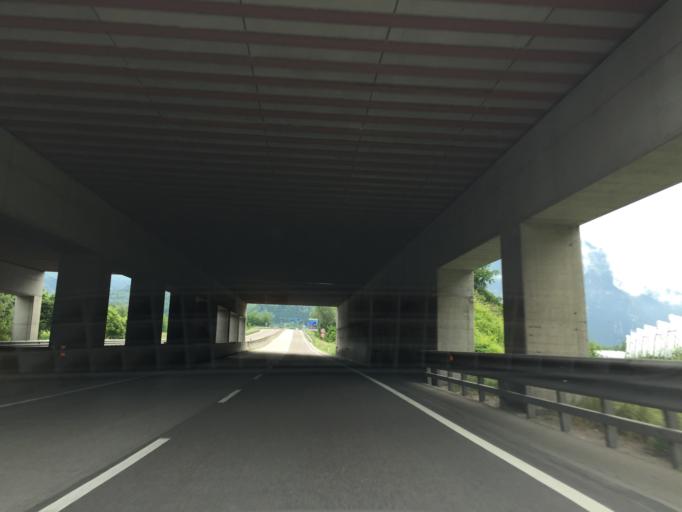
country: IT
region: Trentino-Alto Adige
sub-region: Provincia di Trento
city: Castelnuovo
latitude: 46.0505
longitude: 11.5020
